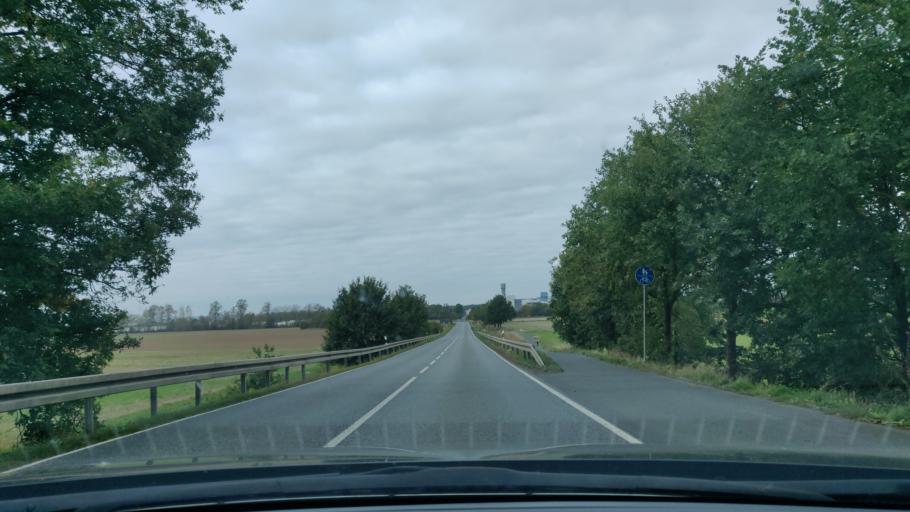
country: DE
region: Hesse
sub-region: Regierungsbezirk Kassel
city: Wabern
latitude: 51.0946
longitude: 9.3688
